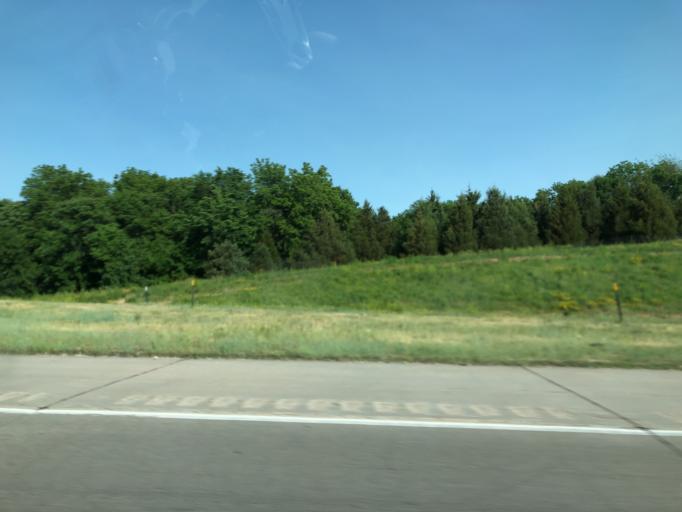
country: US
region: Nebraska
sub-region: Saunders County
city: Ashland
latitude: 41.0086
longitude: -96.3104
